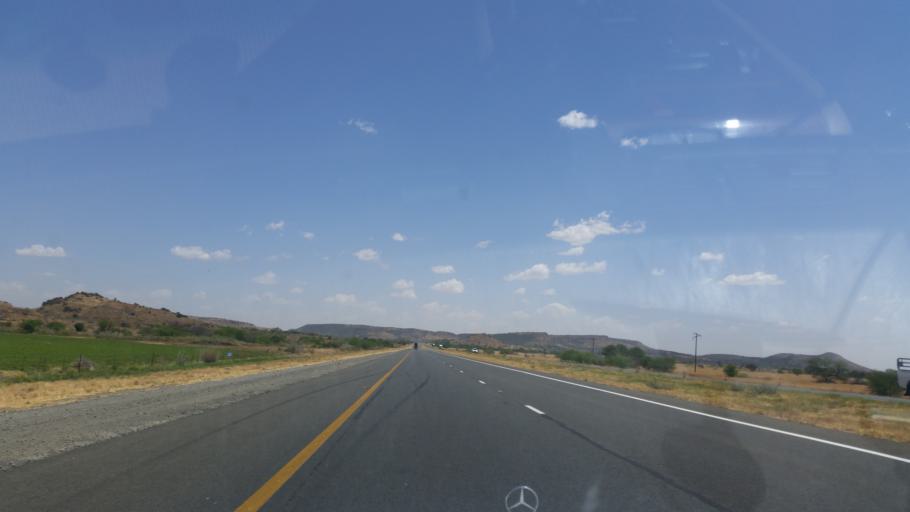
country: ZA
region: Orange Free State
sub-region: Mangaung Metropolitan Municipality
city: Bloemfontein
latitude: -28.9699
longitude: 26.3265
